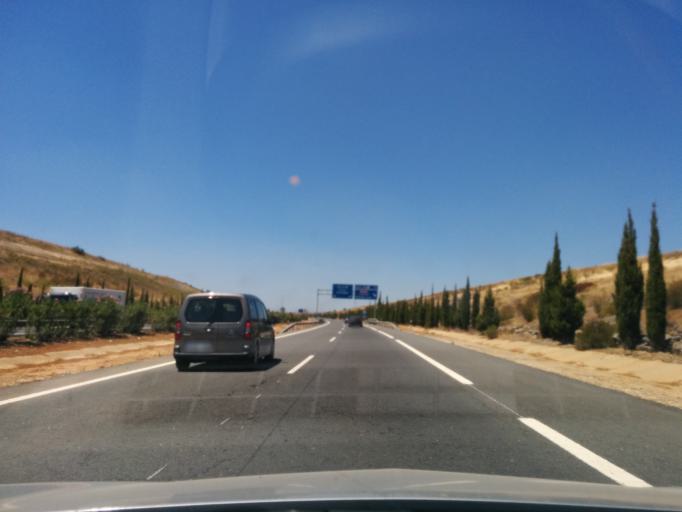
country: ES
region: Andalusia
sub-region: Provincia de Huelva
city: Gibraleon
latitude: 37.3558
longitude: -6.9417
